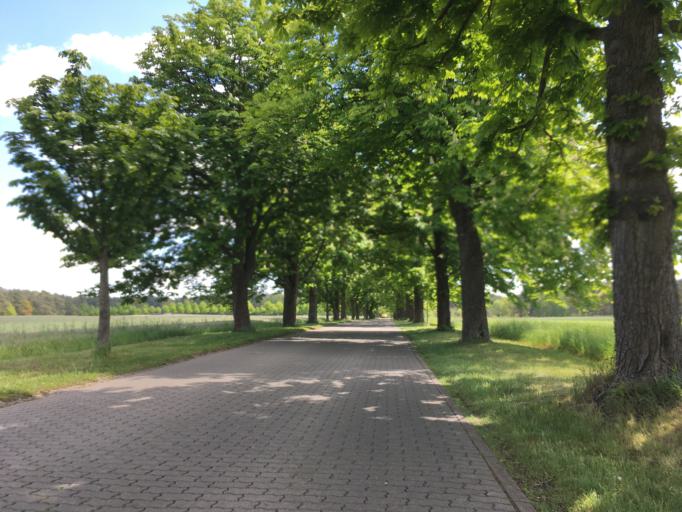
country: DE
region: Brandenburg
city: Biesenthal
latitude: 52.7522
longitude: 13.6467
